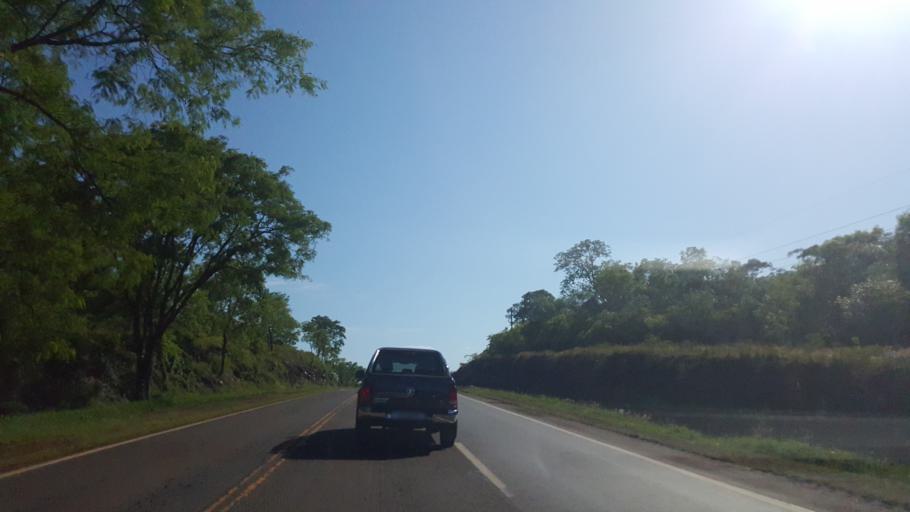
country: AR
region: Misiones
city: Santa Ana
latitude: -27.3571
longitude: -55.5559
